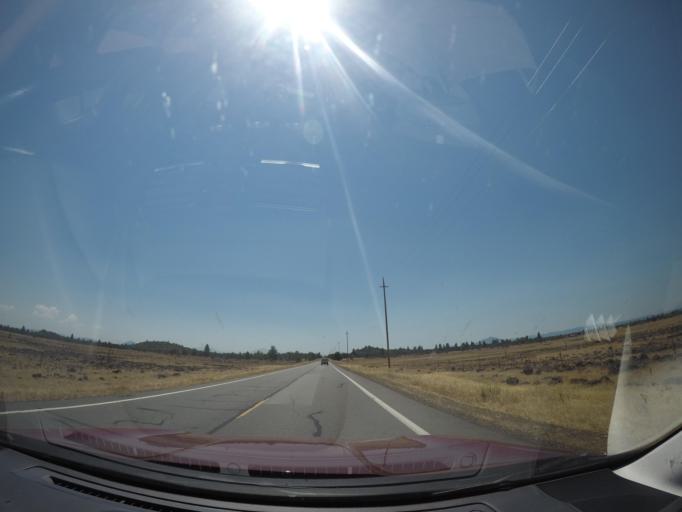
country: US
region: California
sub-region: Shasta County
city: Burney
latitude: 41.0978
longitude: -121.2978
